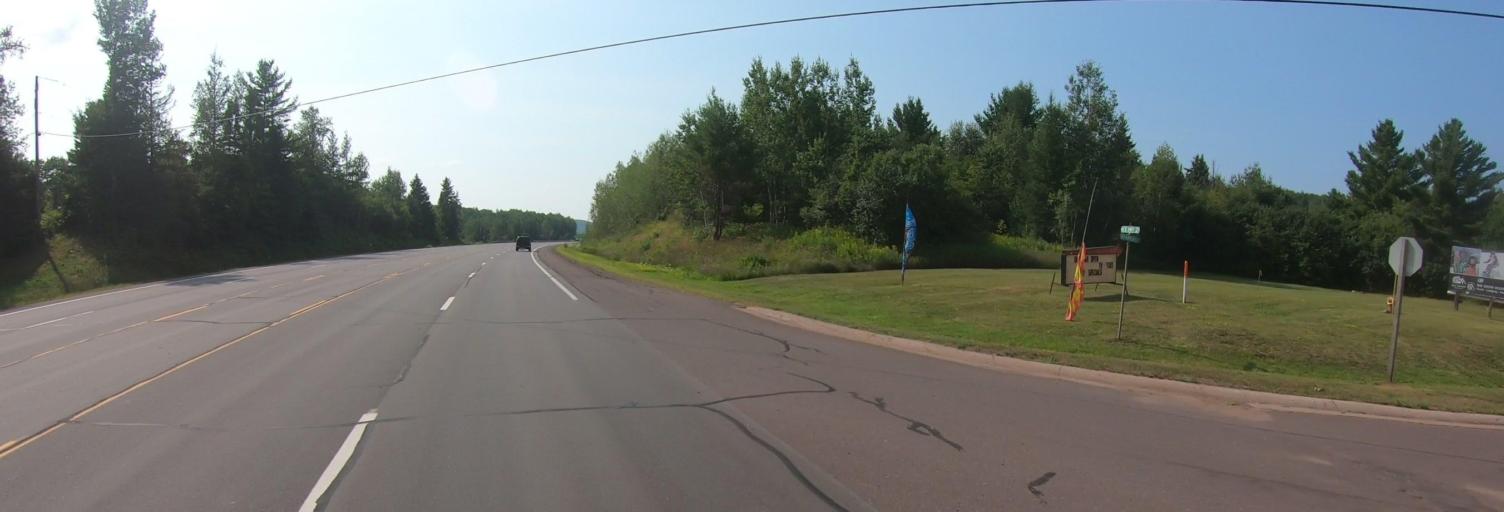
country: US
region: Michigan
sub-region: Gogebic County
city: Wakefield
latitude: 46.4779
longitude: -89.9703
